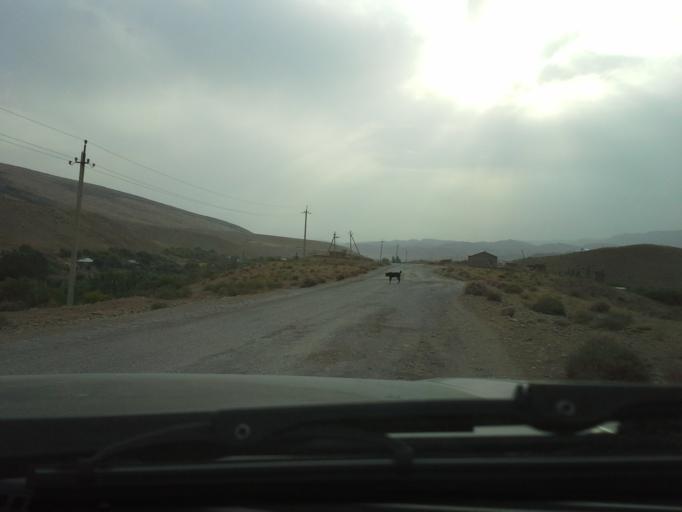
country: UZ
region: Qashqadaryo
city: Qorashina
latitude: 37.9360
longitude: 66.5138
